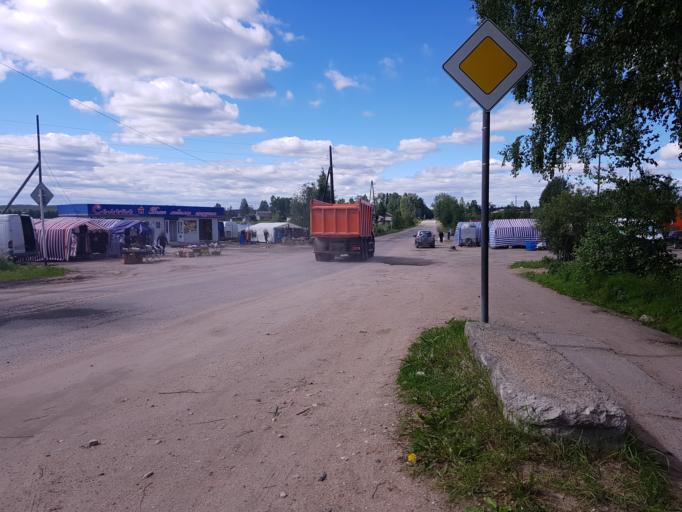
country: RU
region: Republic of Karelia
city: Kalevala
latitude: 65.1979
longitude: 31.1804
